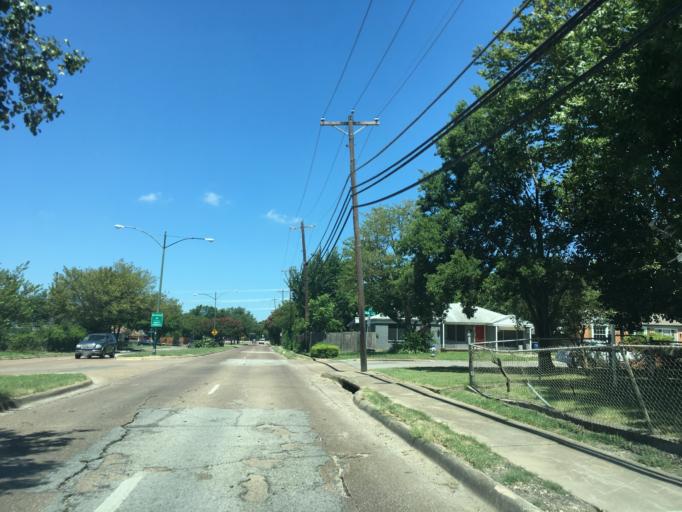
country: US
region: Texas
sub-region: Dallas County
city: Garland
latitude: 32.8390
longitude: -96.6835
